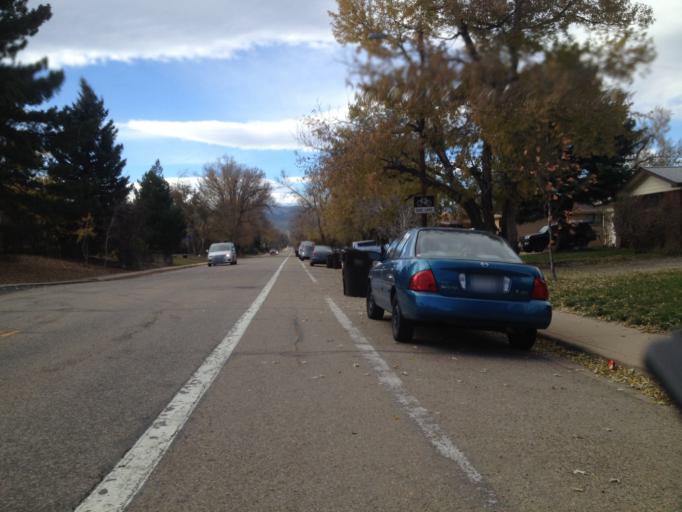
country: US
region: Colorado
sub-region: Boulder County
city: Boulder
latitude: 39.9924
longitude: -105.2465
